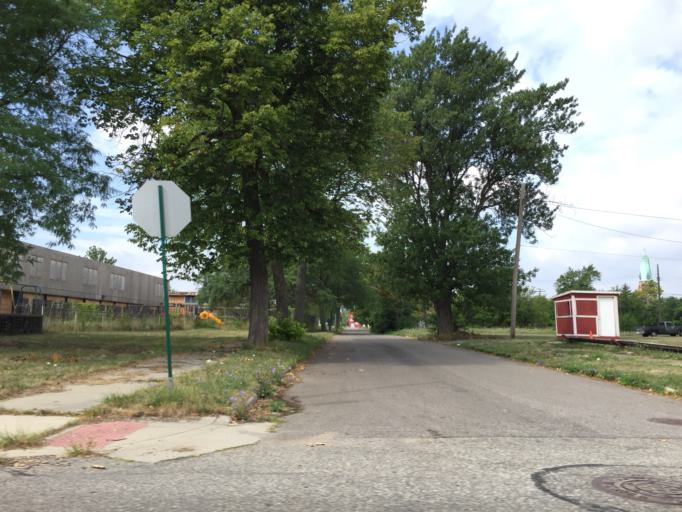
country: US
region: Michigan
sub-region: Wayne County
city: Detroit
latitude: 42.3599
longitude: -83.0371
